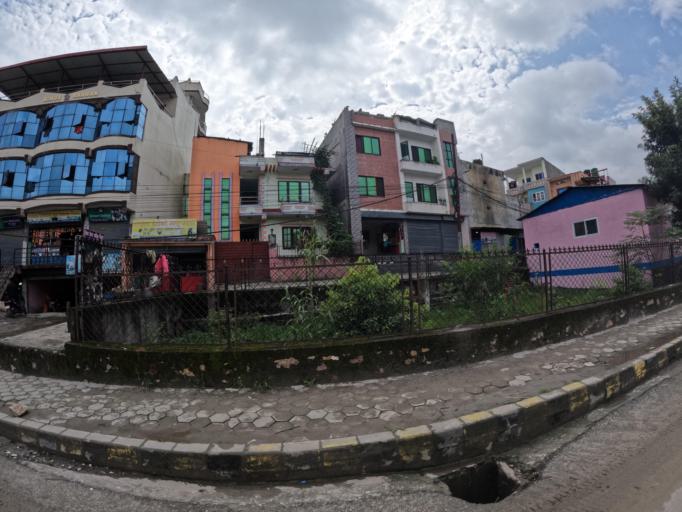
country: NP
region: Central Region
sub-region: Bagmati Zone
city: Kathmandu
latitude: 27.7540
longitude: 85.3167
